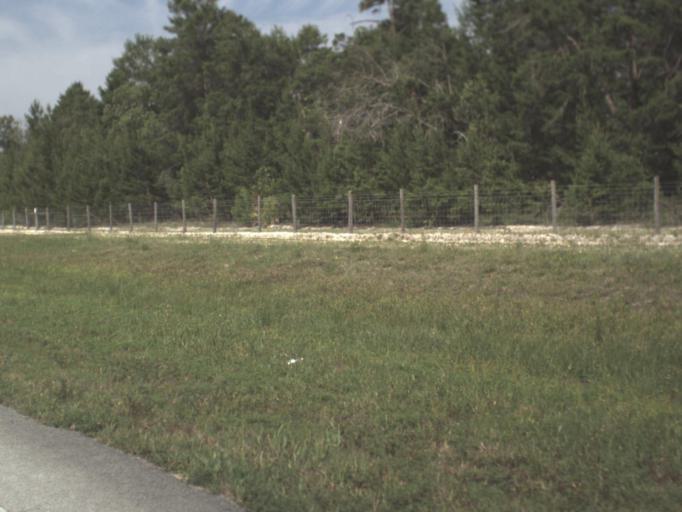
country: US
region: Florida
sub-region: Bradford County
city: Starke
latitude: 29.9420
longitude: -82.0170
